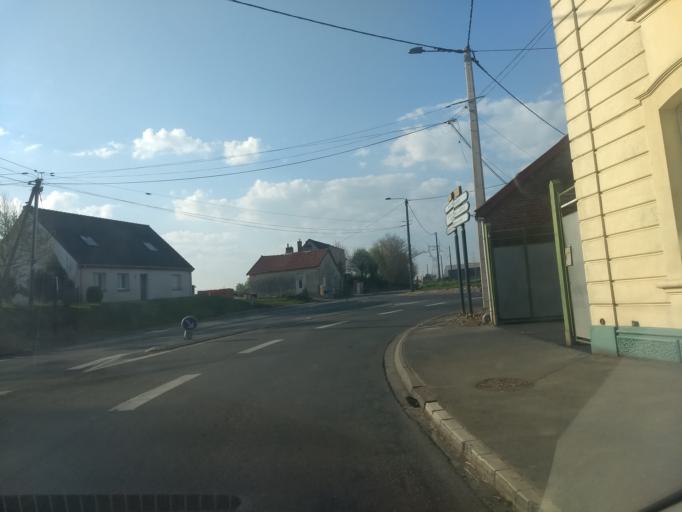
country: FR
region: Nord-Pas-de-Calais
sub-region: Departement du Pas-de-Calais
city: Bucquoy
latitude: 50.1135
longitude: 2.6932
